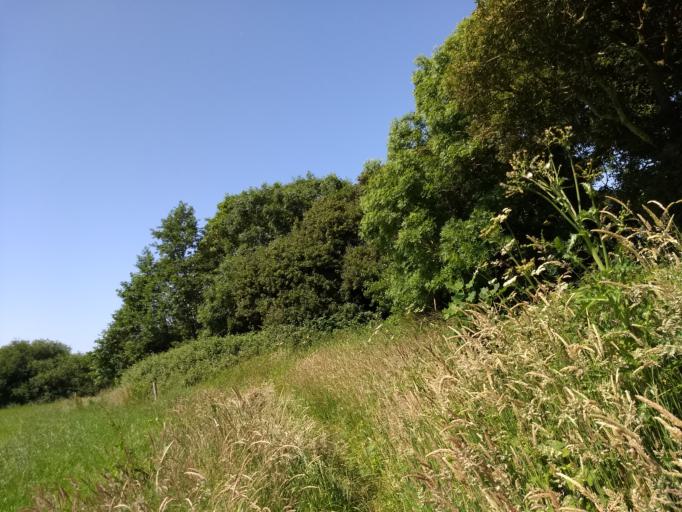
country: GB
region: England
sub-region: Isle of Wight
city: Shalfleet
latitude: 50.6956
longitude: -1.4149
